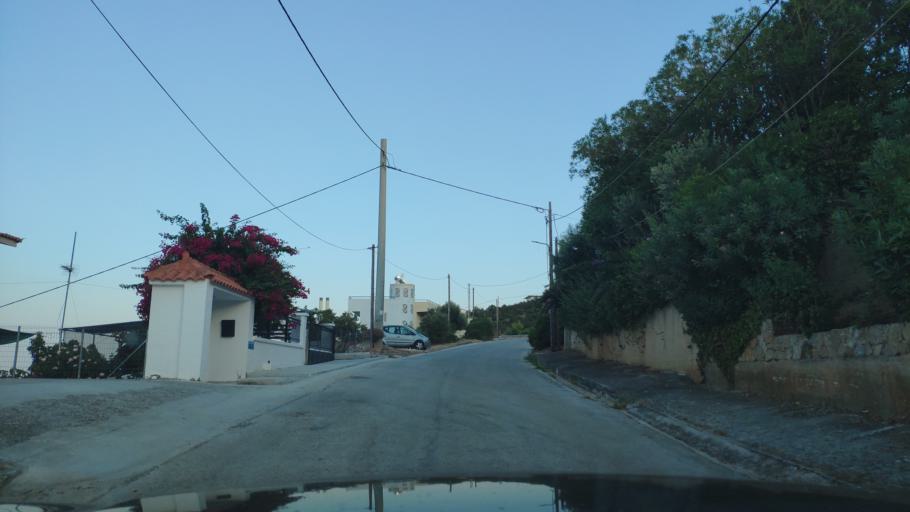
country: GR
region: Attica
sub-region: Nomarchia Anatolikis Attikis
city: Limin Mesoyaias
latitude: 37.9161
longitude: 24.0222
